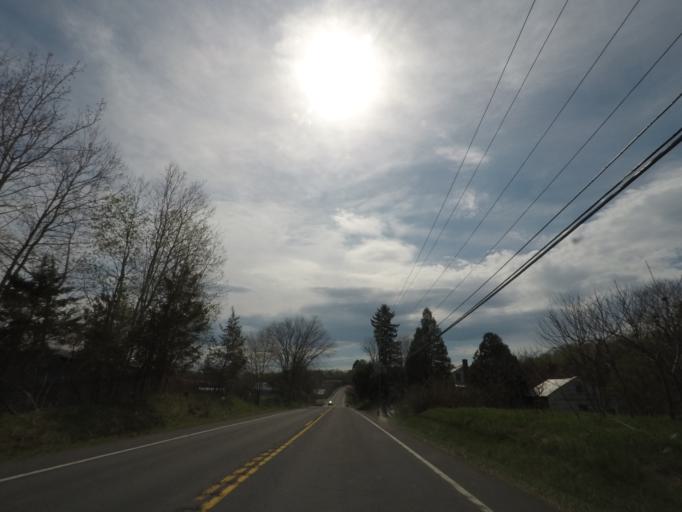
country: US
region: New York
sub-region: Columbia County
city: Philmont
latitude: 42.3002
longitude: -73.6594
